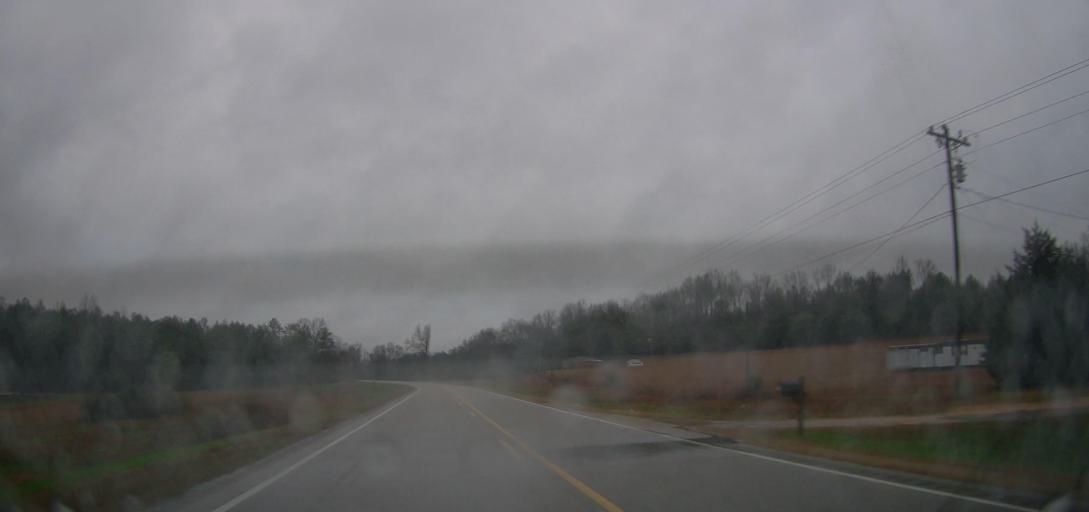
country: US
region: Alabama
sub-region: Autauga County
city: Pine Level
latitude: 32.5247
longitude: -86.6274
